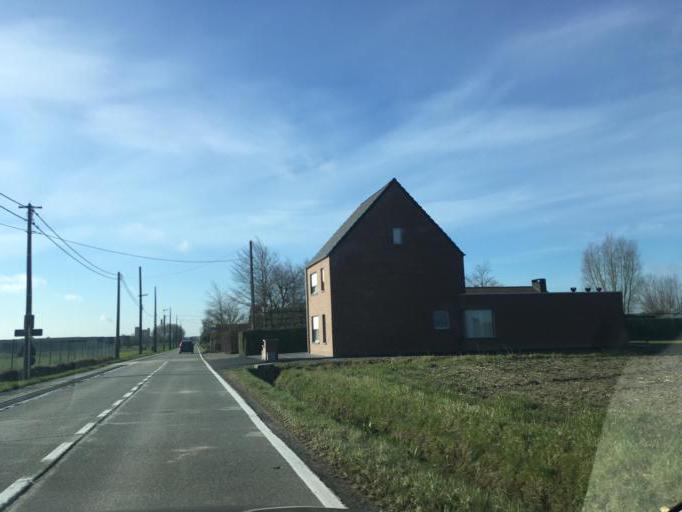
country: BE
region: Flanders
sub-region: Provincie West-Vlaanderen
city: Ledegem
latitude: 50.8876
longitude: 3.1479
